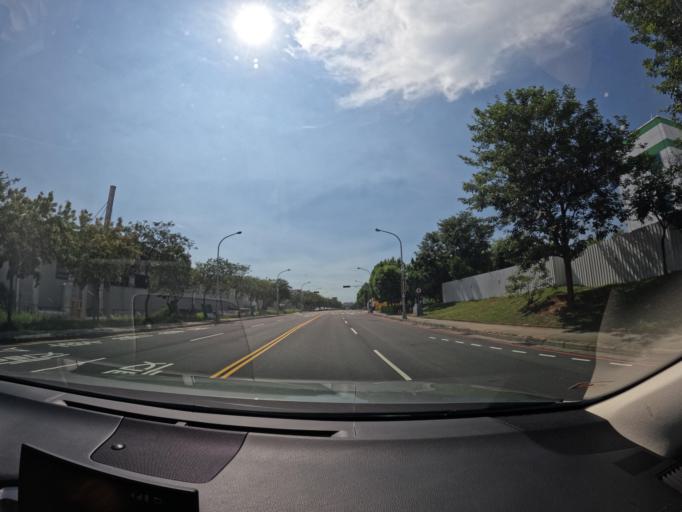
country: TW
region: Taiwan
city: Fengyuan
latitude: 24.3155
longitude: 120.7281
